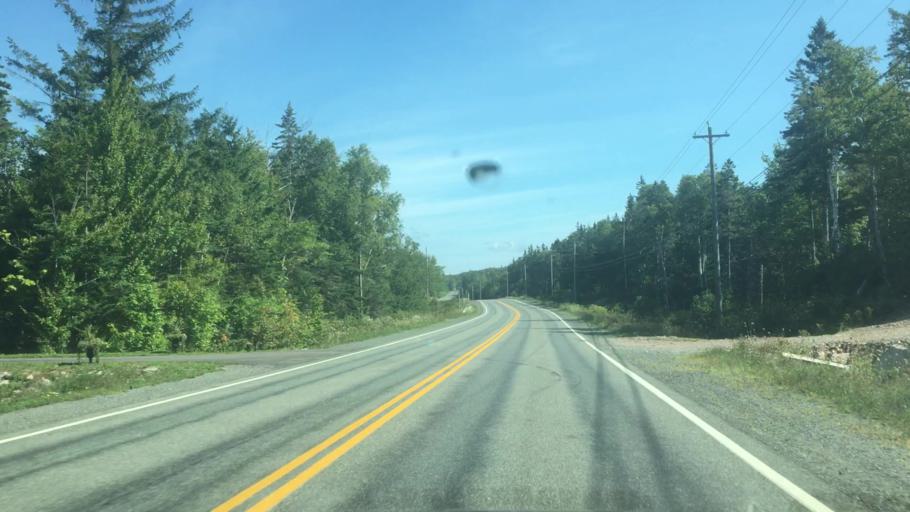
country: CA
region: Nova Scotia
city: Sydney
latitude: 45.9890
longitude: -60.4147
